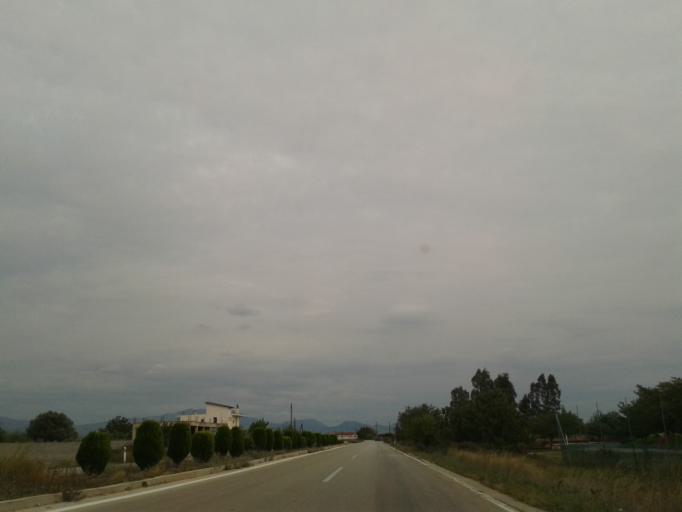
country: GR
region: Peloponnese
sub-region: Nomos Argolidos
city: Argos
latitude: 37.6151
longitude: 22.7220
